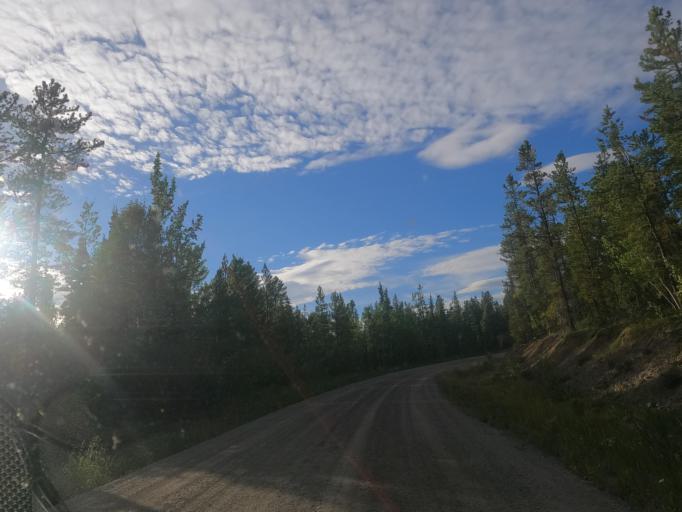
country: CA
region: Yukon
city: Whitehorse
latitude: 60.7551
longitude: -135.0367
